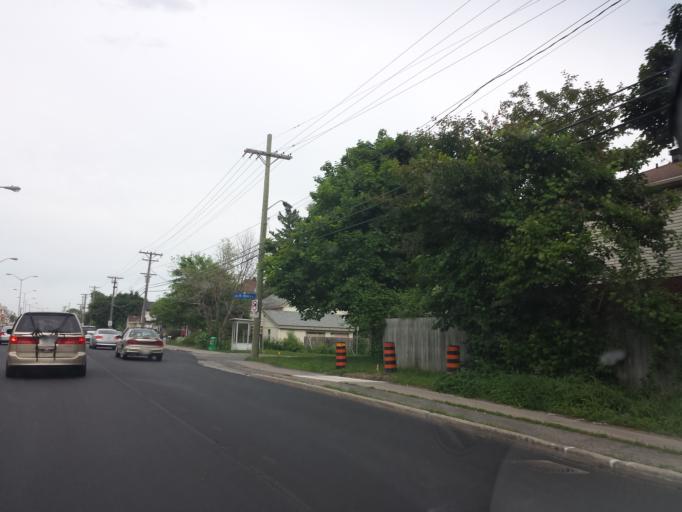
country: CA
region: Ontario
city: Ottawa
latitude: 45.3598
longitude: -75.7432
